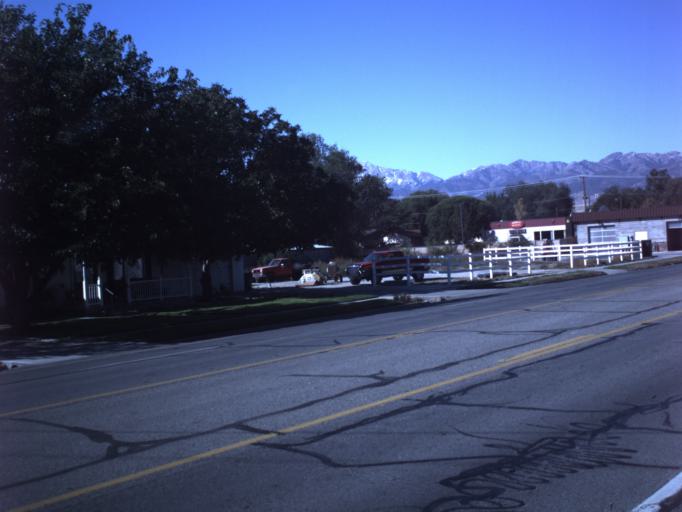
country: US
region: Utah
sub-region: Tooele County
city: Grantsville
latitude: 40.5999
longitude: -112.4546
